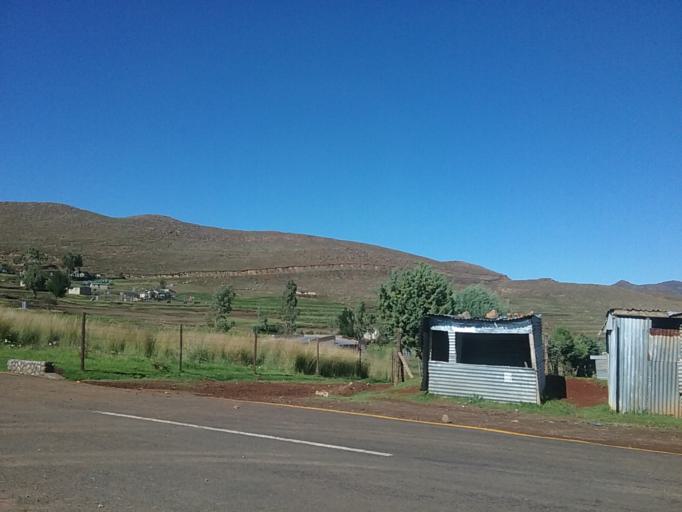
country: LS
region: Berea
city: Teyateyaneng
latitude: -29.2286
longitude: 27.8667
